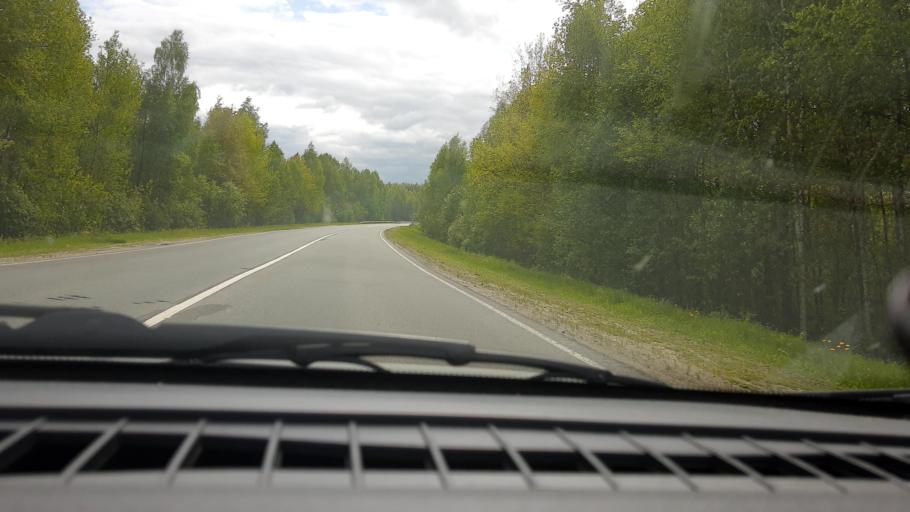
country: RU
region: Nizjnij Novgorod
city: Semenov
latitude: 56.7982
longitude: 44.4600
